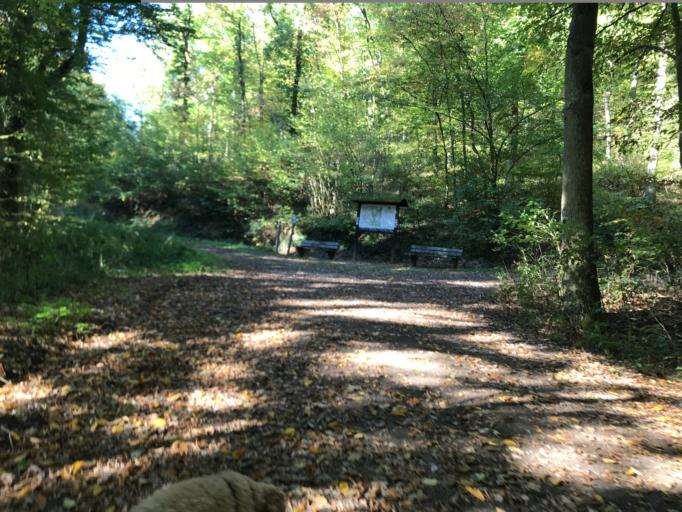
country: DE
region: Rheinland-Pfalz
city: Wolken
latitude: 50.3269
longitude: 7.4455
